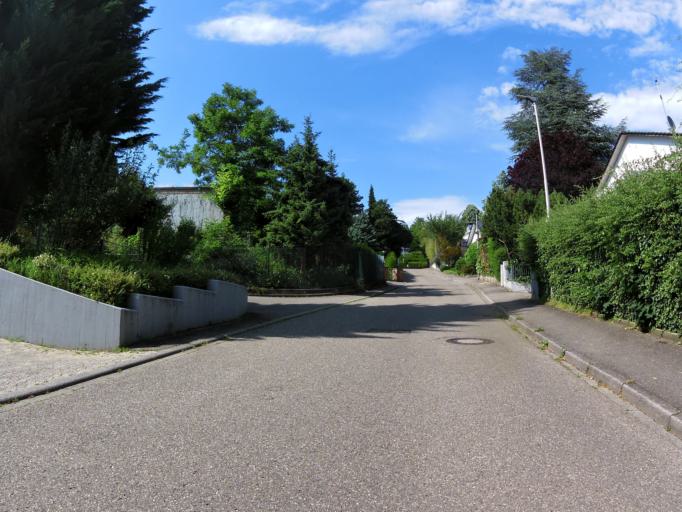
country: DE
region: Baden-Wuerttemberg
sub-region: Freiburg Region
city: Lahr
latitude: 48.3438
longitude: 7.8566
